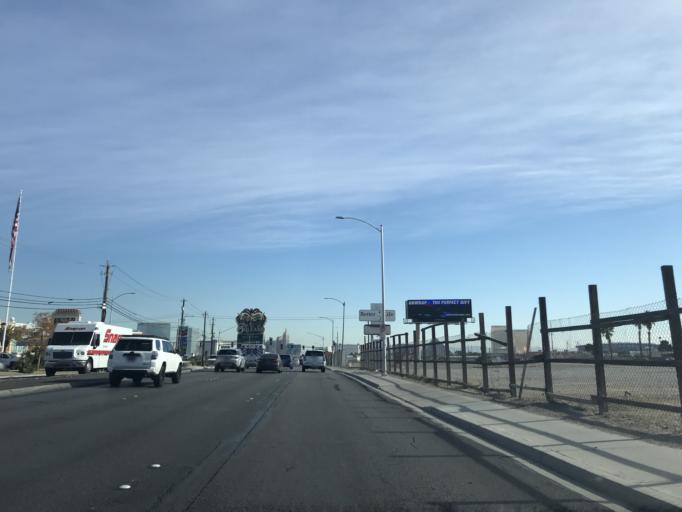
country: US
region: Nevada
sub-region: Clark County
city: Spring Valley
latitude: 36.1008
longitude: -115.2059
